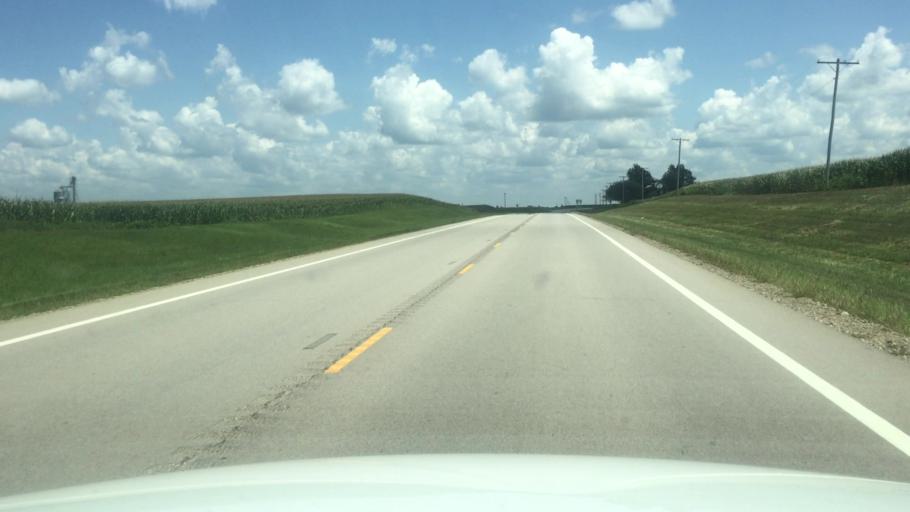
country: US
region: Kansas
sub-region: Brown County
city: Horton
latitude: 39.6673
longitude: -95.4308
